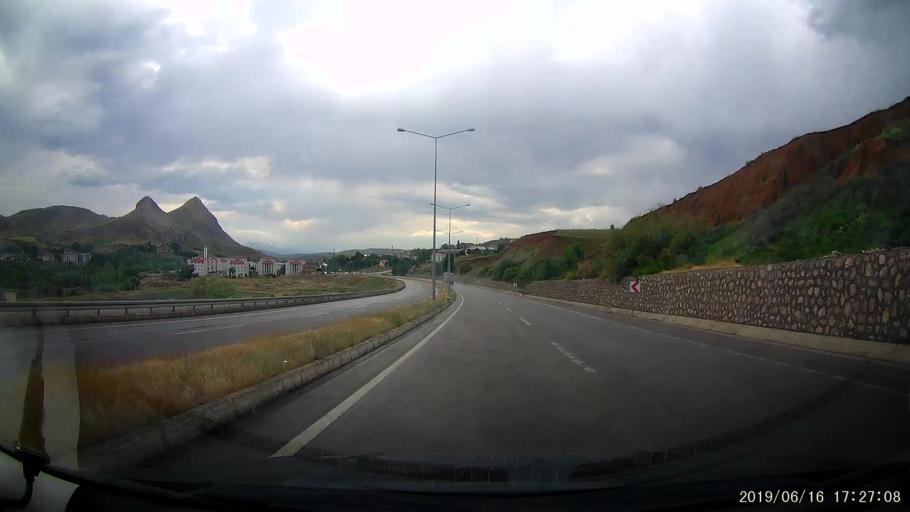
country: TR
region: Erzincan
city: Tercan
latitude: 39.7750
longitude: 40.3989
